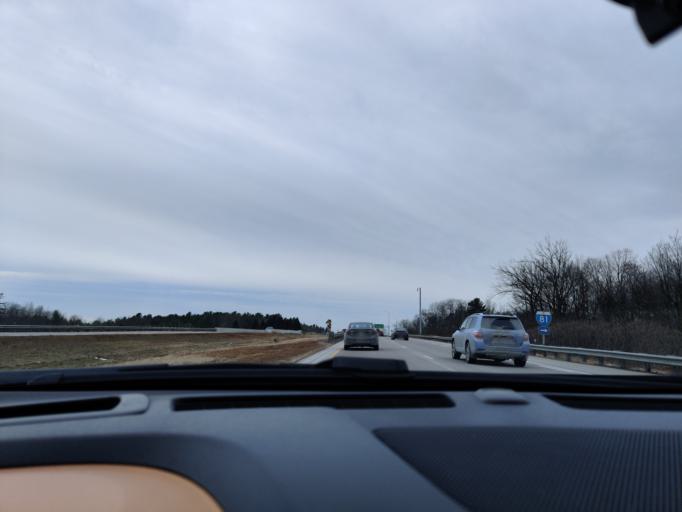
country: US
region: New York
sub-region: Jefferson County
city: Alexandria Bay
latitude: 44.3827
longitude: -75.9812
